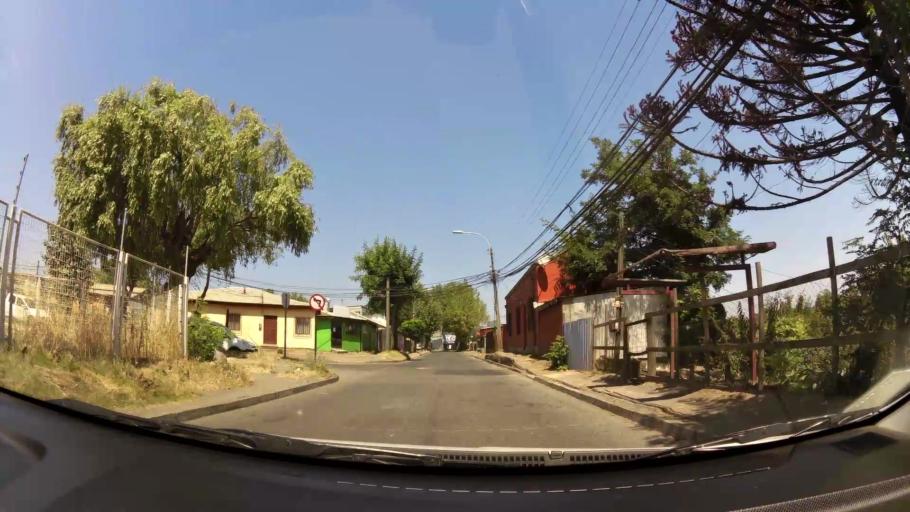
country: CL
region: Biobio
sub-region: Provincia de Concepcion
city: Concepcion
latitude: -36.8070
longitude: -73.0539
